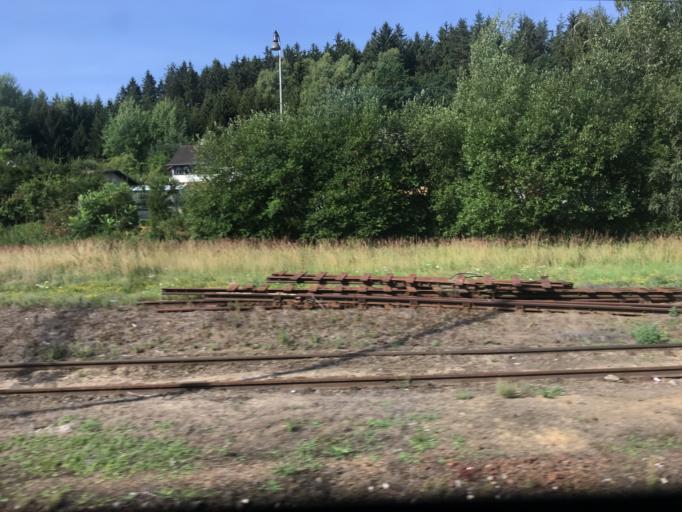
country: CZ
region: Central Bohemia
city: Votice
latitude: 49.5784
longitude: 14.6062
